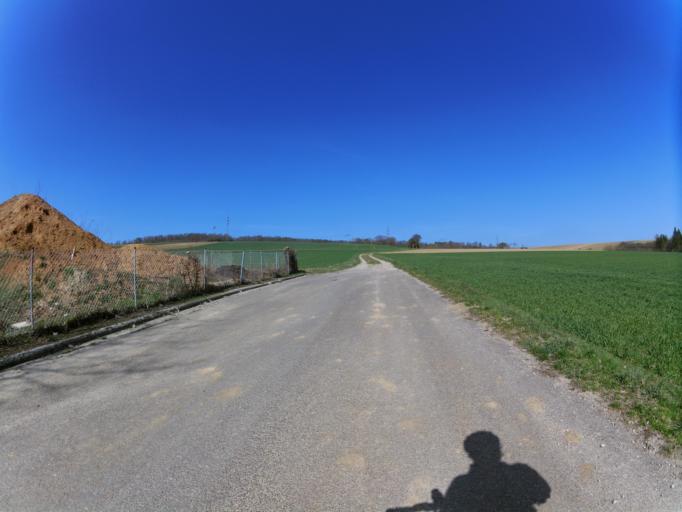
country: DE
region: Bavaria
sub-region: Regierungsbezirk Unterfranken
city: Greussenheim
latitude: 49.8009
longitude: 9.7583
